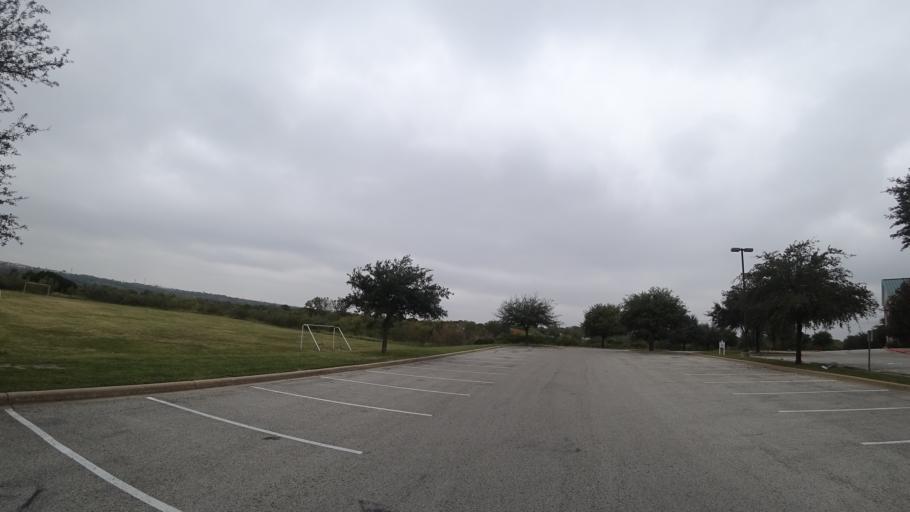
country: US
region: Texas
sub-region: Travis County
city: Pflugerville
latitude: 30.3830
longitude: -97.6539
